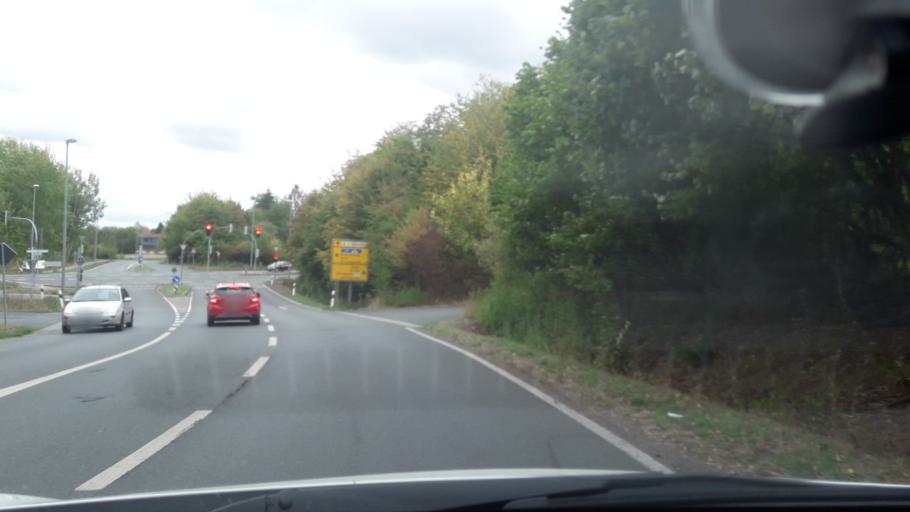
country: DE
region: Lower Saxony
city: Cramme
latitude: 52.0997
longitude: 10.3657
